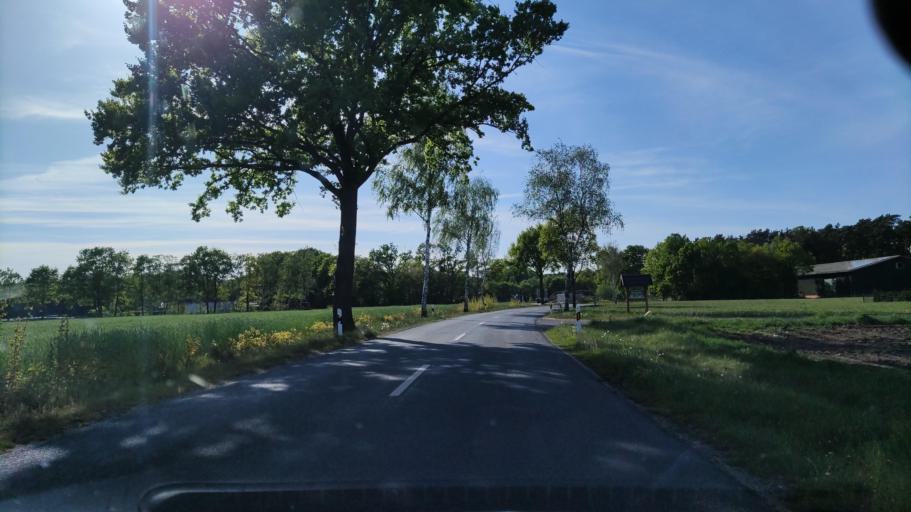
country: DE
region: Lower Saxony
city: Schneverdingen
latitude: 53.1751
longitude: 9.8015
